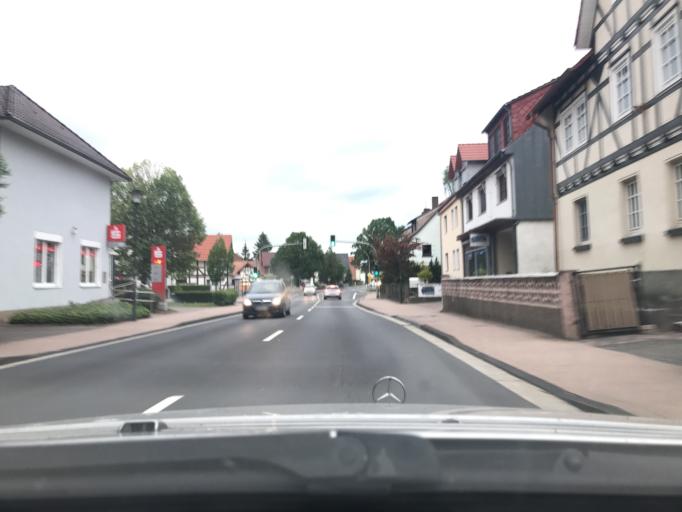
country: DE
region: Hesse
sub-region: Regierungsbezirk Kassel
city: Eschwege
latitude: 51.1542
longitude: 9.9989
